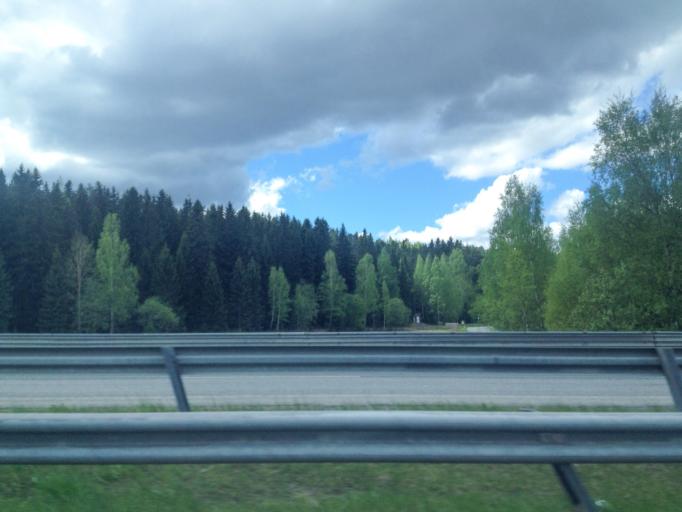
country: FI
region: Haeme
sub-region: Haemeenlinna
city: Haemeenlinna
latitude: 60.9753
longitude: 24.4716
